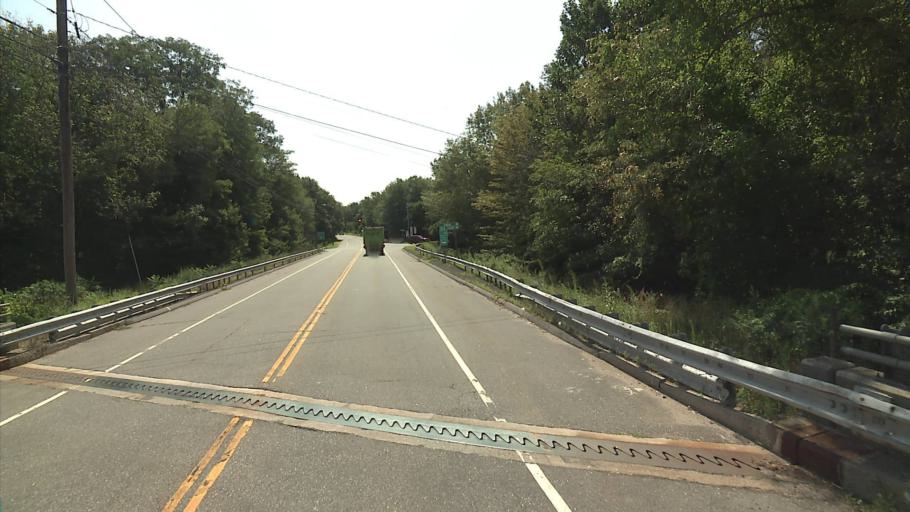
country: US
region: Connecticut
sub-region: New London County
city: Colchester
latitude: 41.5625
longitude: -72.3161
